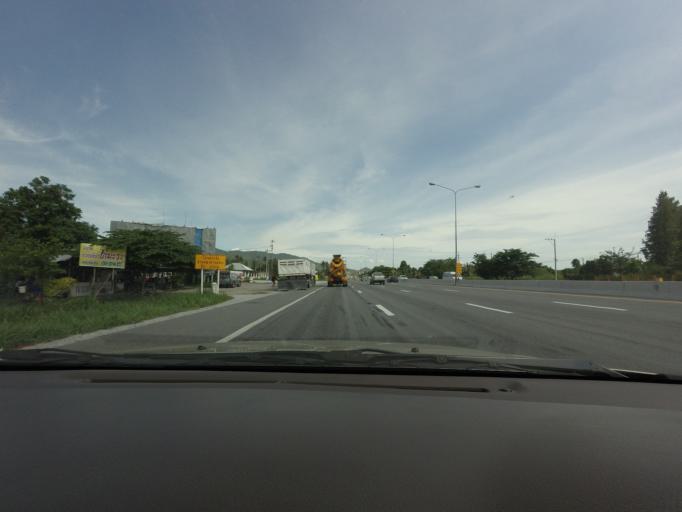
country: TH
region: Chon Buri
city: Chon Buri
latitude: 13.3161
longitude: 100.9921
